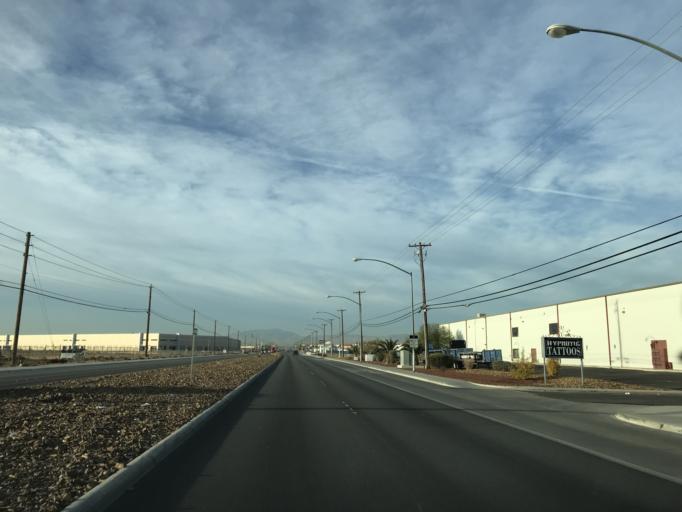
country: US
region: Nevada
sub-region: Clark County
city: Sunrise Manor
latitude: 36.2303
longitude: -115.0720
